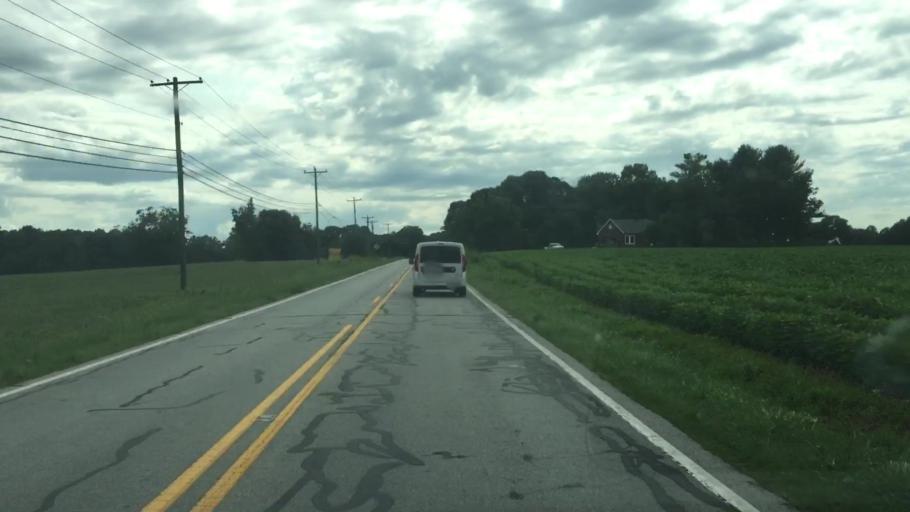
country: US
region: North Carolina
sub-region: Rowan County
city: Franklin
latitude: 35.6605
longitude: -80.5607
